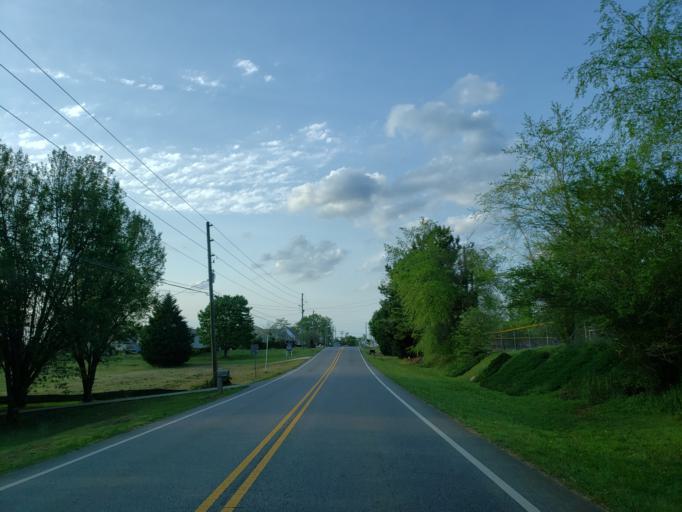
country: US
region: Georgia
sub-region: Cherokee County
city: Ball Ground
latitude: 34.2503
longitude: -84.3592
